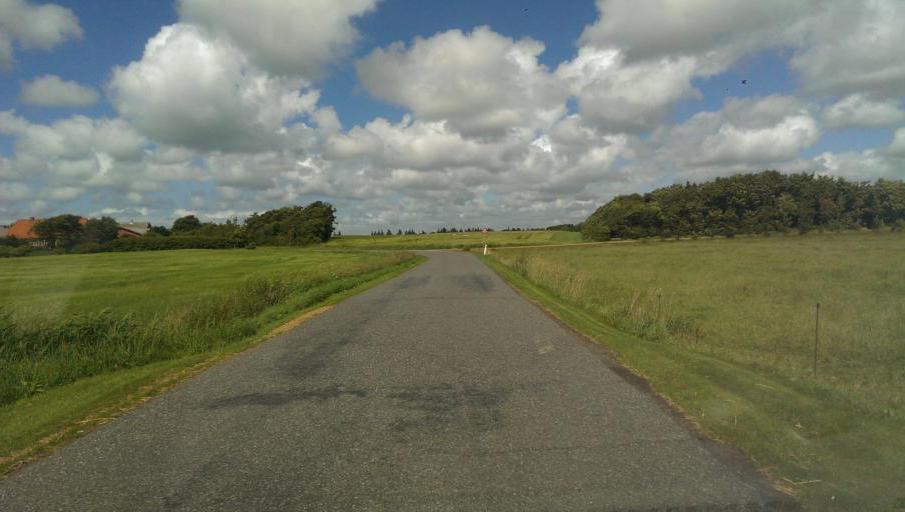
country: DK
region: Central Jutland
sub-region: Holstebro Kommune
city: Ulfborg
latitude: 56.2430
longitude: 8.2362
